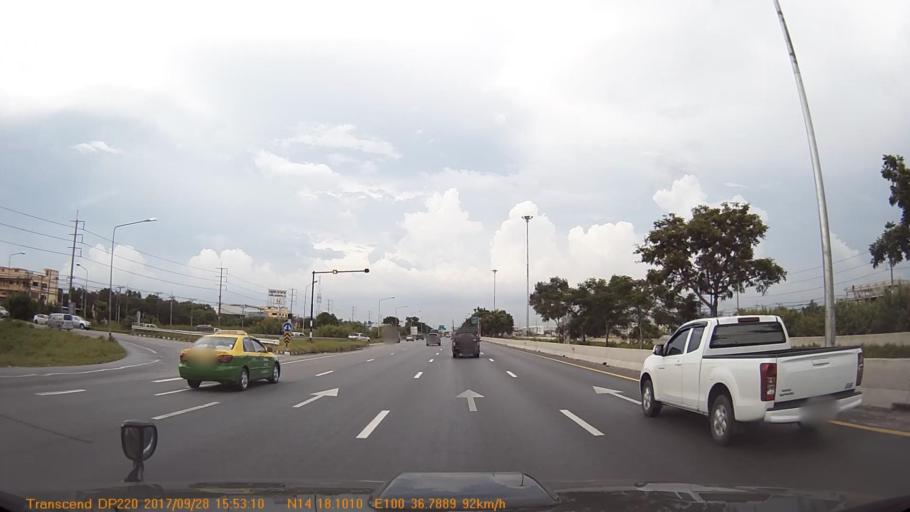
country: TH
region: Phra Nakhon Si Ayutthaya
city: Phra Nakhon Si Ayutthaya
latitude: 14.3020
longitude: 100.6131
